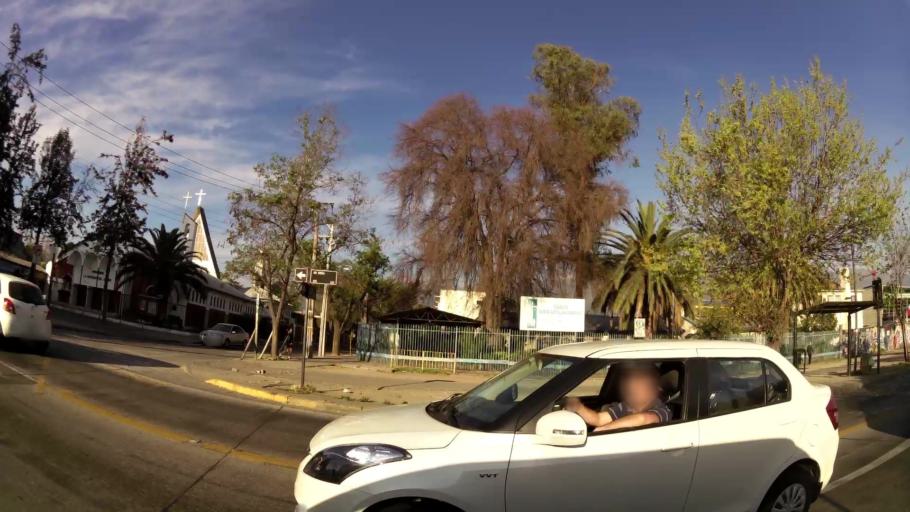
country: CL
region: Santiago Metropolitan
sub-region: Provincia de Santiago
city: Villa Presidente Frei, Nunoa, Santiago, Chile
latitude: -33.4494
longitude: -70.5713
